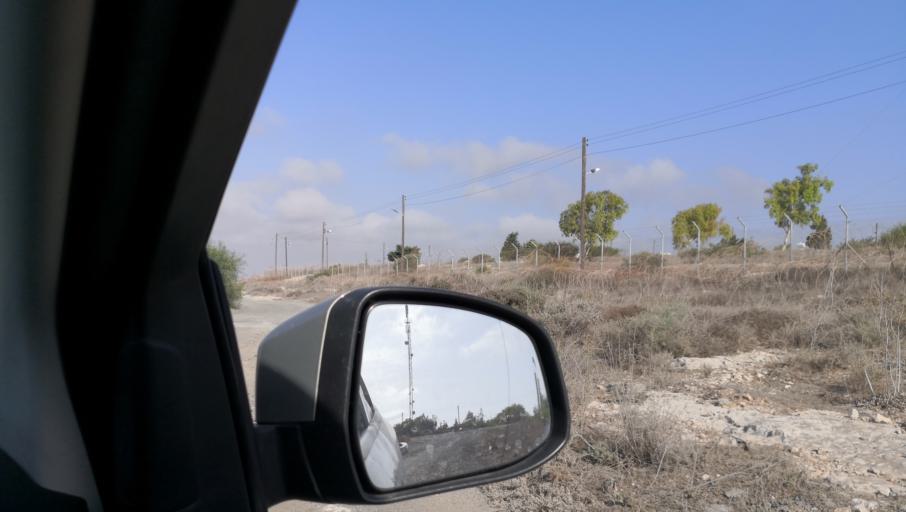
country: CY
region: Ammochostos
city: Protaras
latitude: 35.0046
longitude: 34.0293
